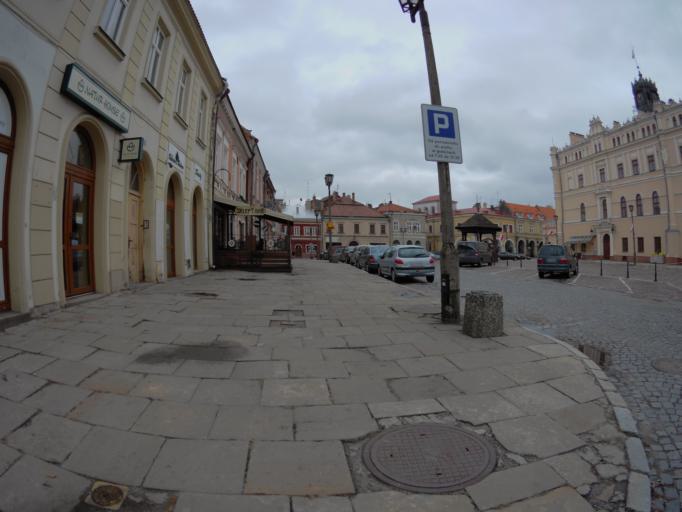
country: PL
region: Subcarpathian Voivodeship
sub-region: Powiat jaroslawski
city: Jaroslaw
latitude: 50.0189
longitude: 22.6828
